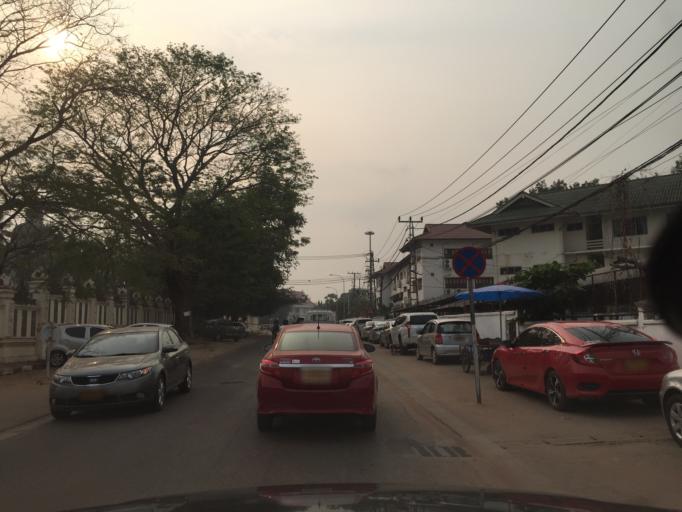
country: LA
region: Vientiane
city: Vientiane
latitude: 17.9713
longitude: 102.6167
